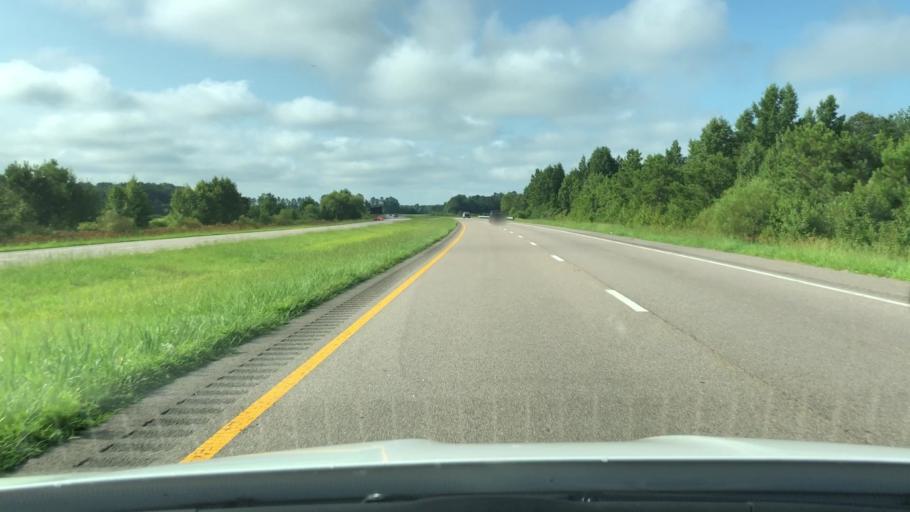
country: US
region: Virginia
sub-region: City of Portsmouth
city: Portsmouth Heights
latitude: 36.6868
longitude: -76.3475
